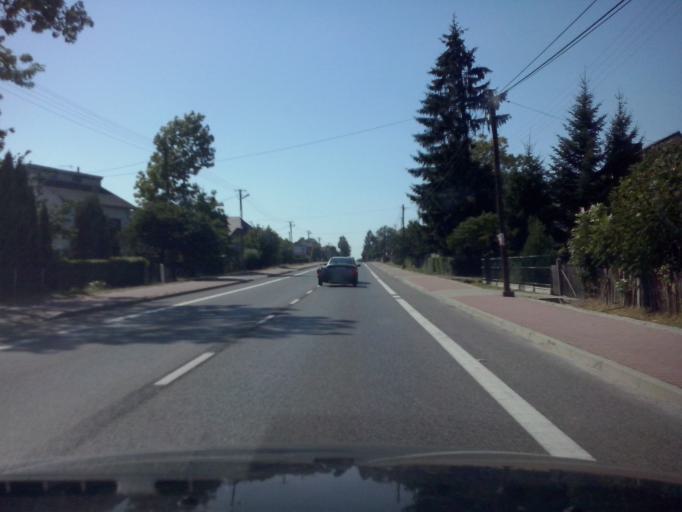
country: PL
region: Swietokrzyskie
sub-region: Powiat kielecki
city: Bieliny
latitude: 50.8493
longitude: 20.9221
